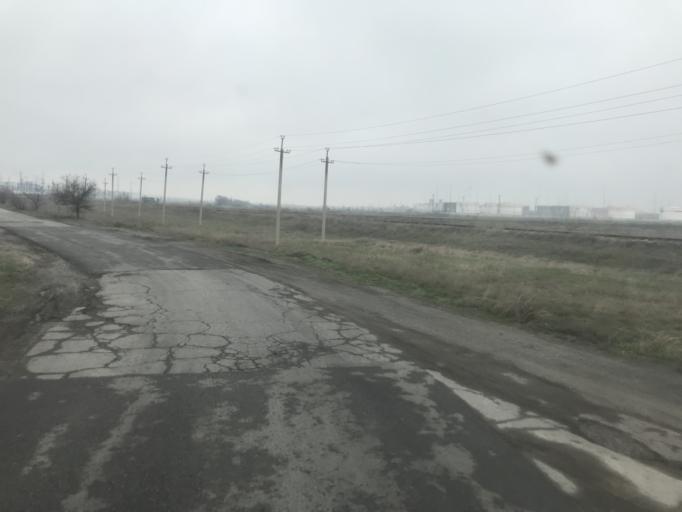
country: RU
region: Volgograd
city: Svetlyy Yar
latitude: 48.4929
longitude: 44.6571
